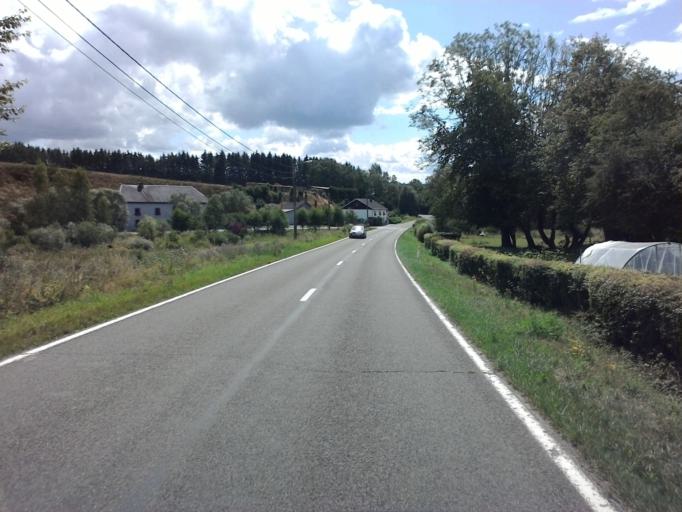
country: BE
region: Wallonia
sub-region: Province du Luxembourg
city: Habay-la-Vieille
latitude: 49.7826
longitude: 5.6068
